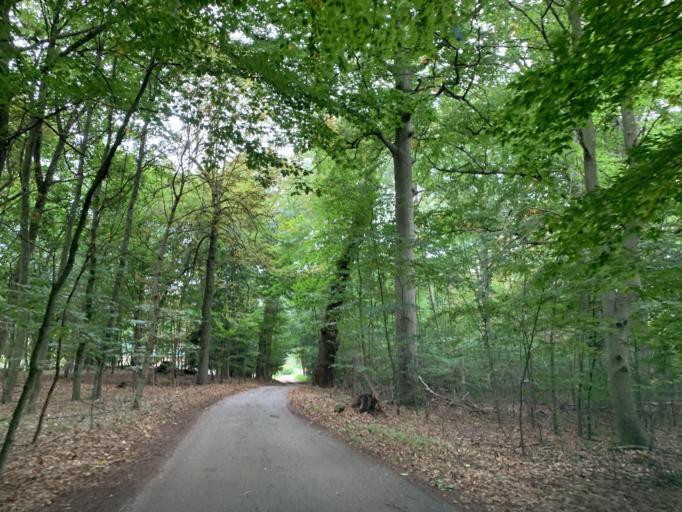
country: DE
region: Brandenburg
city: Mittenwalde
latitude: 53.3160
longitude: 13.6131
